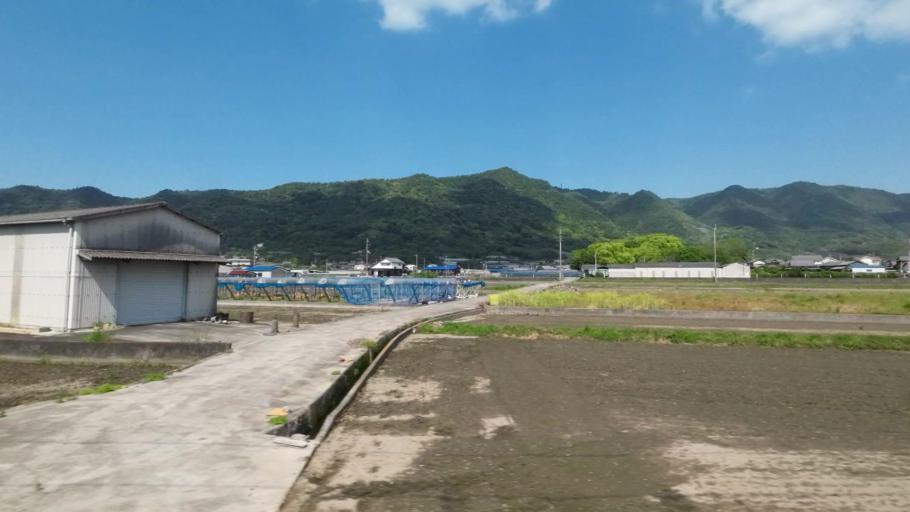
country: JP
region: Kagawa
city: Kan'onjicho
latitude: 34.1558
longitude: 133.6882
